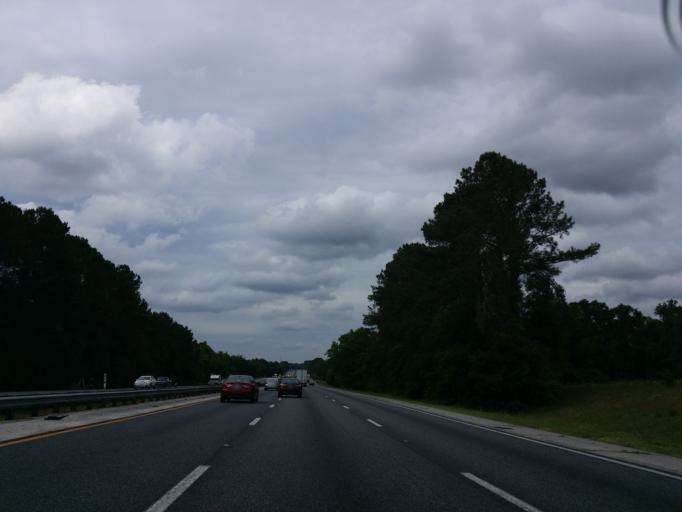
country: US
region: Florida
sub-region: Alachua County
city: High Springs
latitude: 29.9223
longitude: -82.5567
